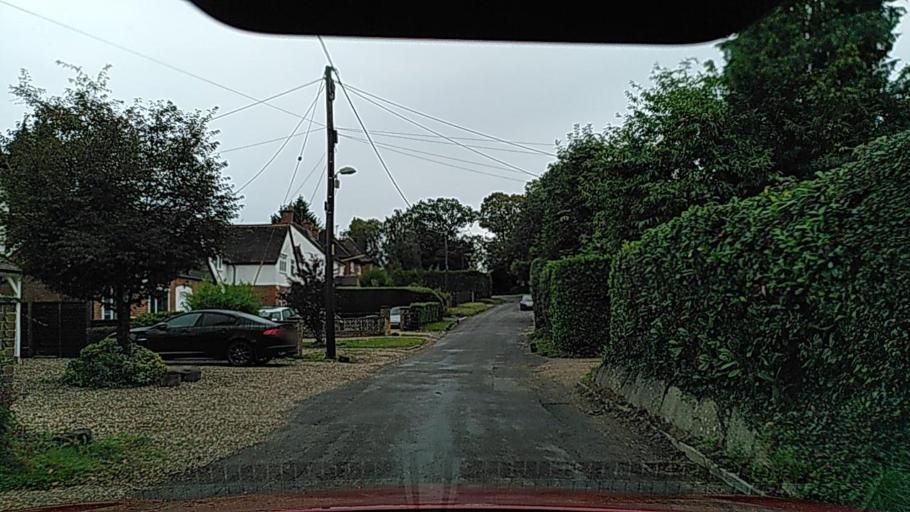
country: GB
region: England
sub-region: Oxfordshire
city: Sonning Common
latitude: 51.5134
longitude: -0.9870
